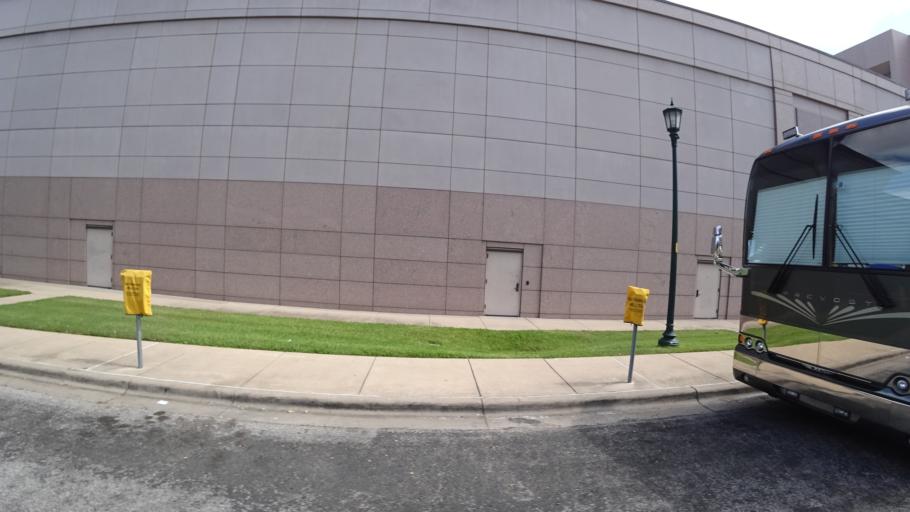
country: US
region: Texas
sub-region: Travis County
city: Austin
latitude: 30.2805
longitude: -97.7397
